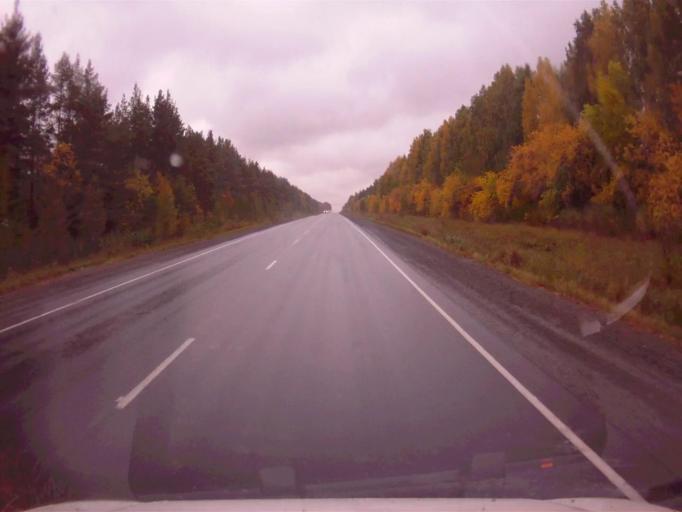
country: RU
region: Chelyabinsk
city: Roshchino
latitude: 55.3764
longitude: 61.1492
